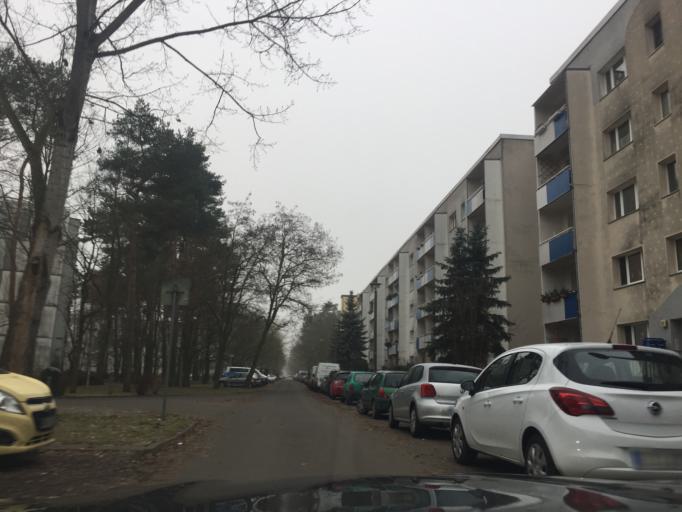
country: DE
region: Brandenburg
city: Hennigsdorf
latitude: 52.6567
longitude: 13.1959
